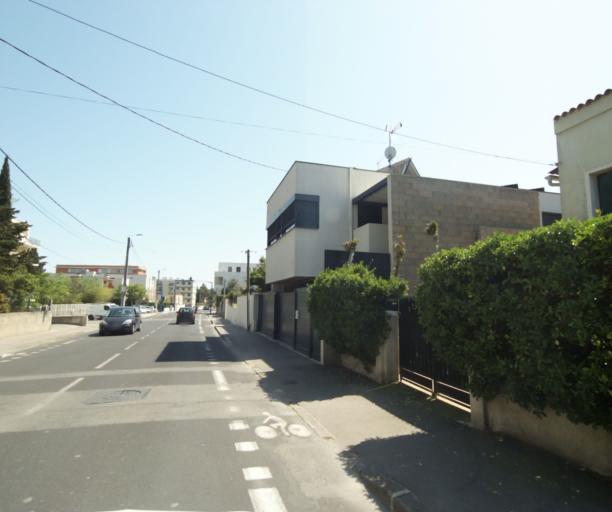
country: FR
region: Languedoc-Roussillon
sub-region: Departement de l'Herault
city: Montpellier
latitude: 43.6249
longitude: 3.8513
